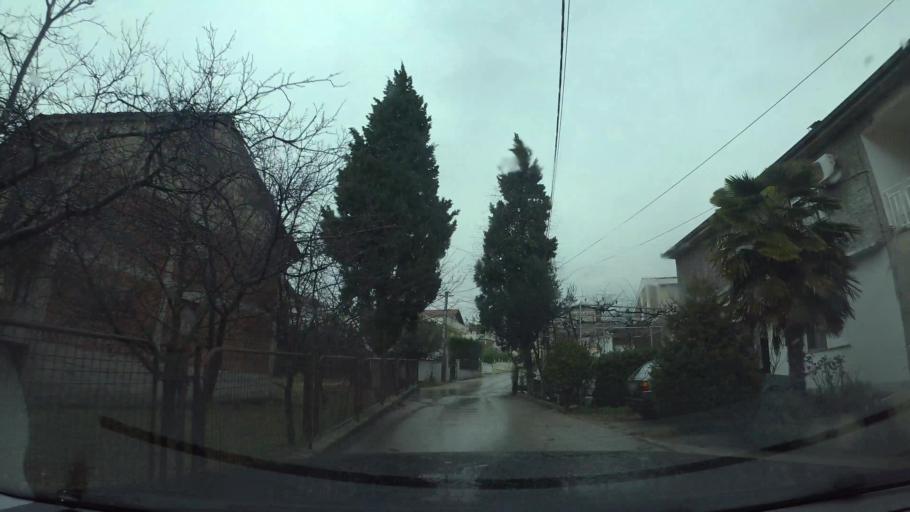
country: BA
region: Federation of Bosnia and Herzegovina
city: Cim
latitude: 43.3490
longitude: 17.7882
